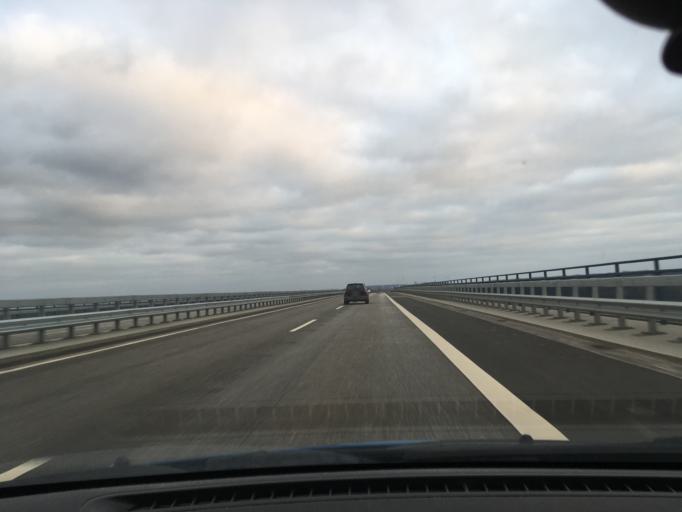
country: DE
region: Schleswig-Holstein
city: Schafstedt
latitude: 54.0702
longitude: 9.3129
